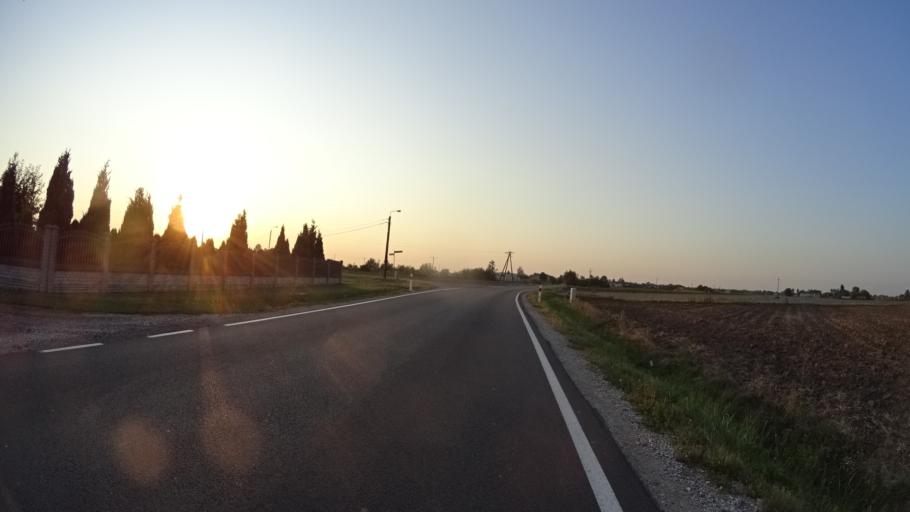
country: PL
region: Masovian Voivodeship
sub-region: Powiat warszawski zachodni
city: Ozarow Mazowiecki
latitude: 52.2402
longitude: 20.7515
